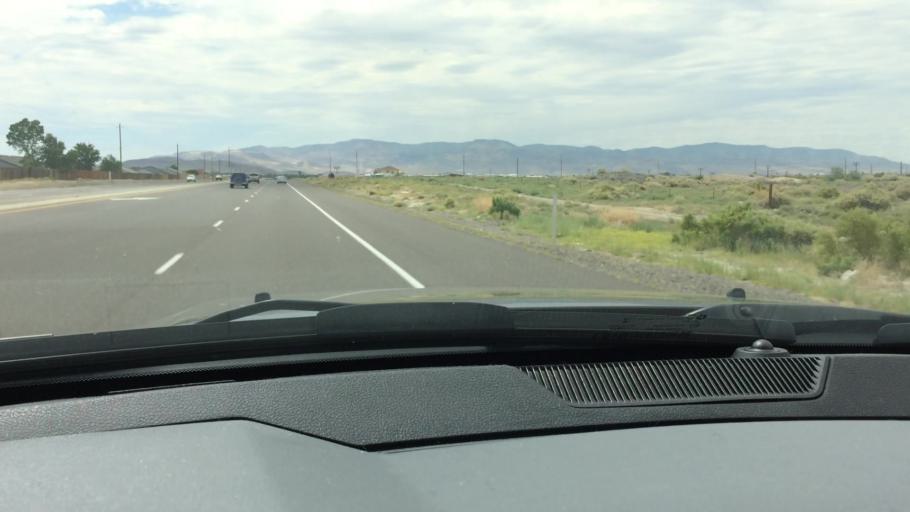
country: US
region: Nevada
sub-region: Lyon County
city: Fernley
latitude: 39.5990
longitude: -119.2011
